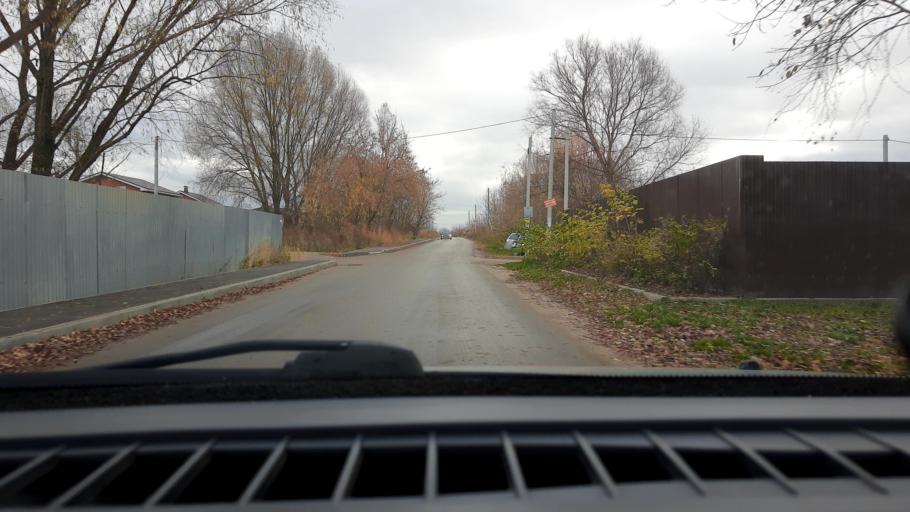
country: RU
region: Nizjnij Novgorod
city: Afonino
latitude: 56.2064
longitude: 44.1259
